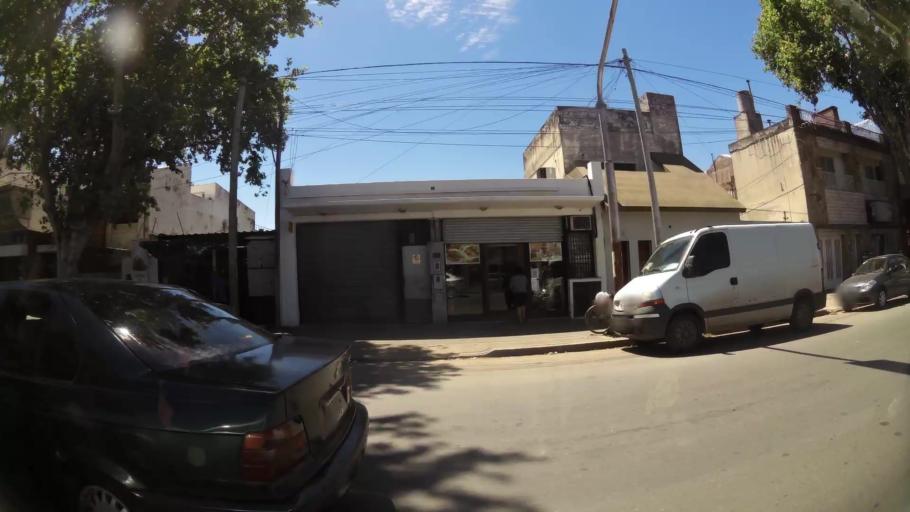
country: AR
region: Santa Fe
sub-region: Departamento de Rosario
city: Rosario
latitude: -32.9491
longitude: -60.7122
